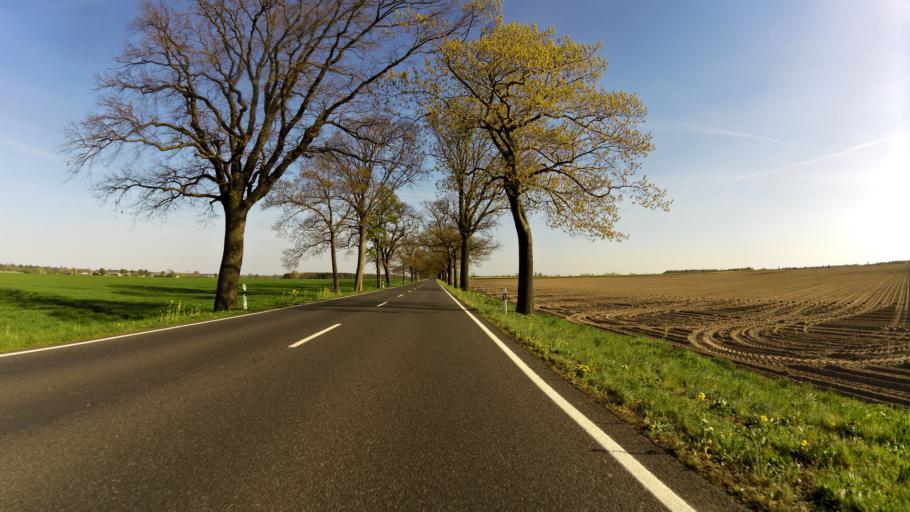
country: DE
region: Brandenburg
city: Pessin
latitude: 52.6708
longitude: 12.6250
